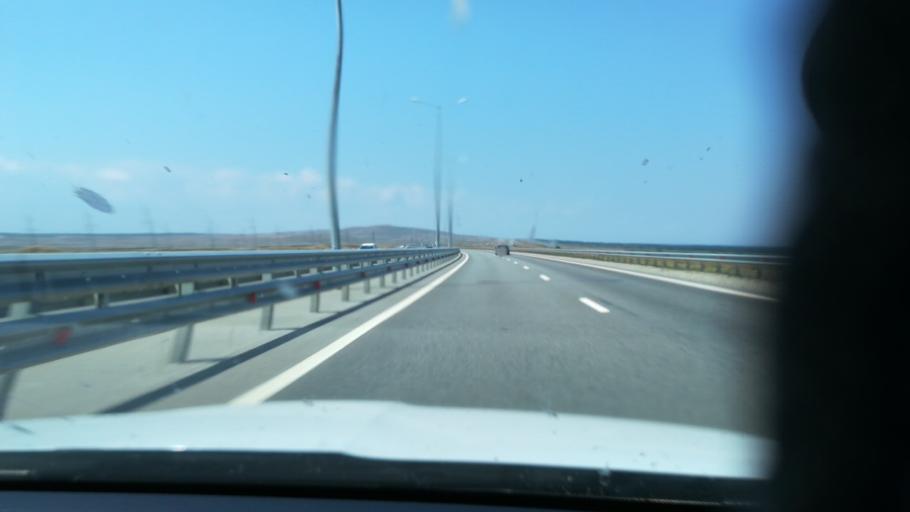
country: RU
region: Krasnodarskiy
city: Vyshestebliyevskaya
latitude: 45.2295
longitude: 36.9519
